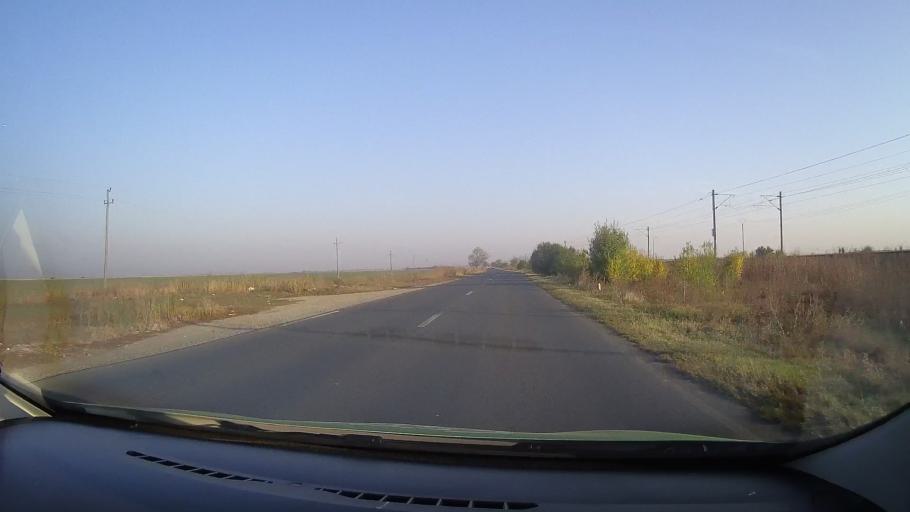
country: RO
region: Arad
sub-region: Comuna Sofronea
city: Sofronea
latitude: 46.2953
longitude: 21.3110
